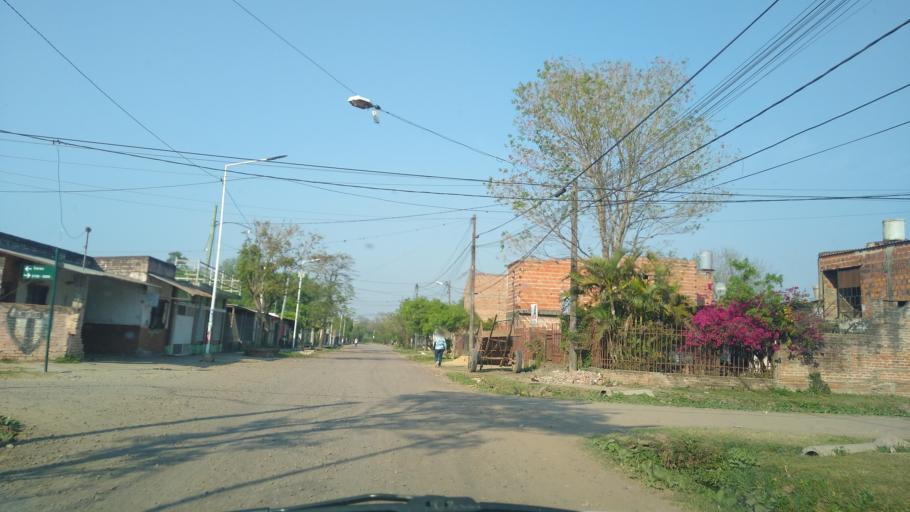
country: AR
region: Chaco
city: Barranqueras
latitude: -27.4749
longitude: -58.9489
